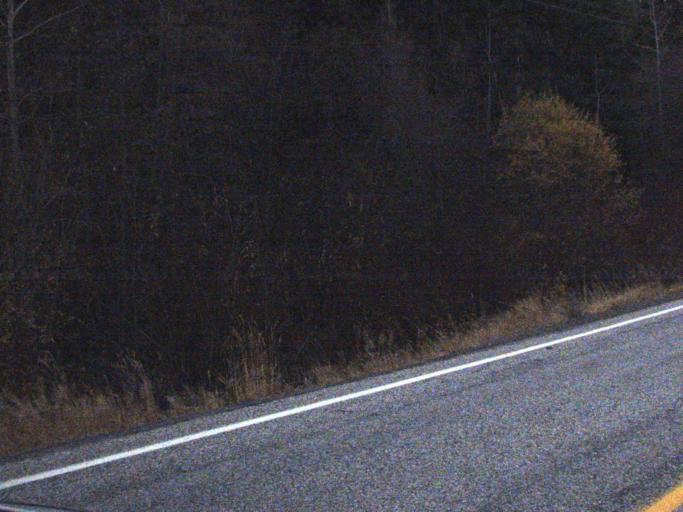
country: US
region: Washington
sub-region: Ferry County
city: Republic
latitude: 48.6288
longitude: -118.6763
